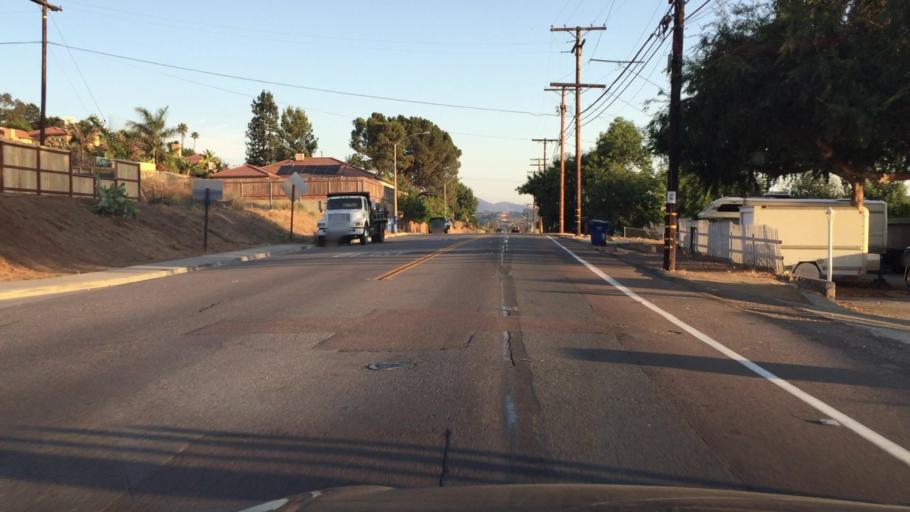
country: US
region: California
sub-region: San Diego County
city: Bostonia
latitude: 32.8186
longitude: -116.9446
